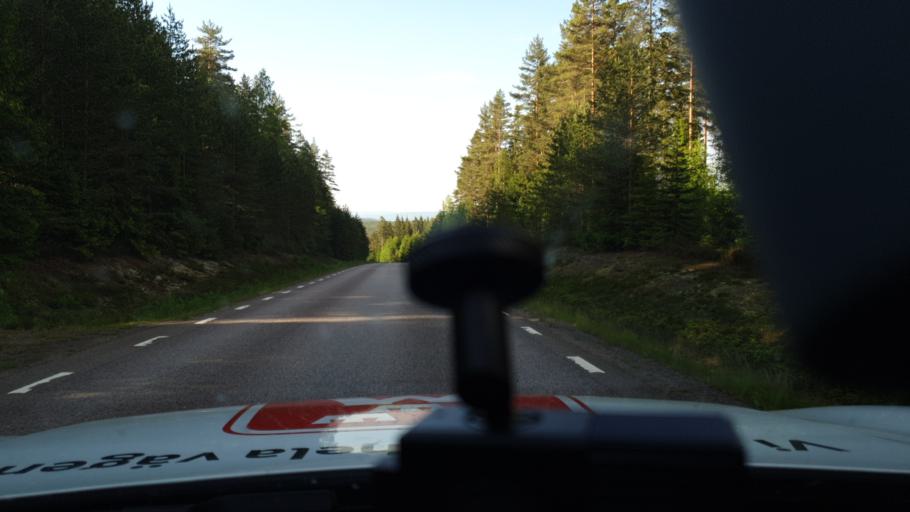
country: SE
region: Vaermland
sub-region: Torsby Kommun
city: Torsby
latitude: 60.0224
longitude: 12.9042
